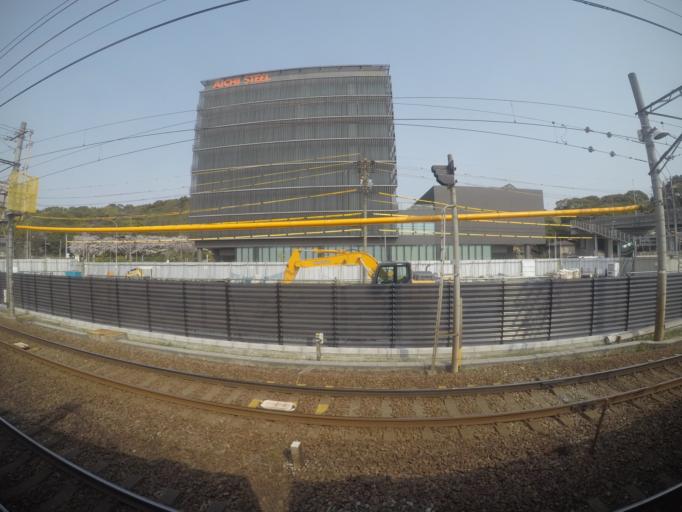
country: JP
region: Aichi
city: Obu
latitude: 35.0416
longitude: 136.9029
